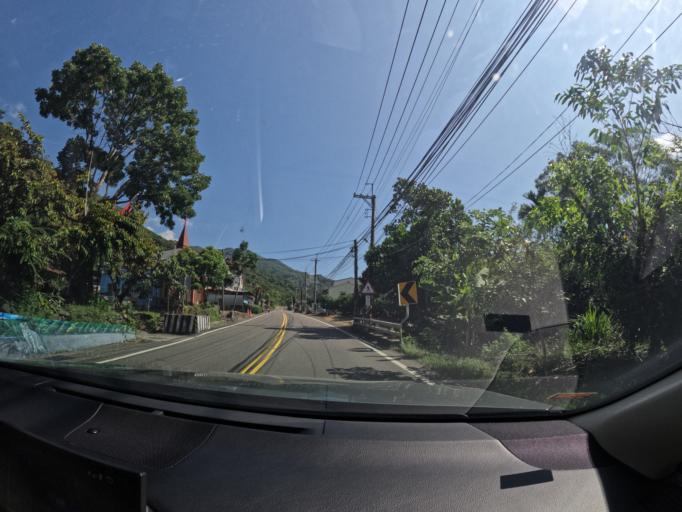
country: TW
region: Taiwan
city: Yujing
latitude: 23.1300
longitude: 120.7187
